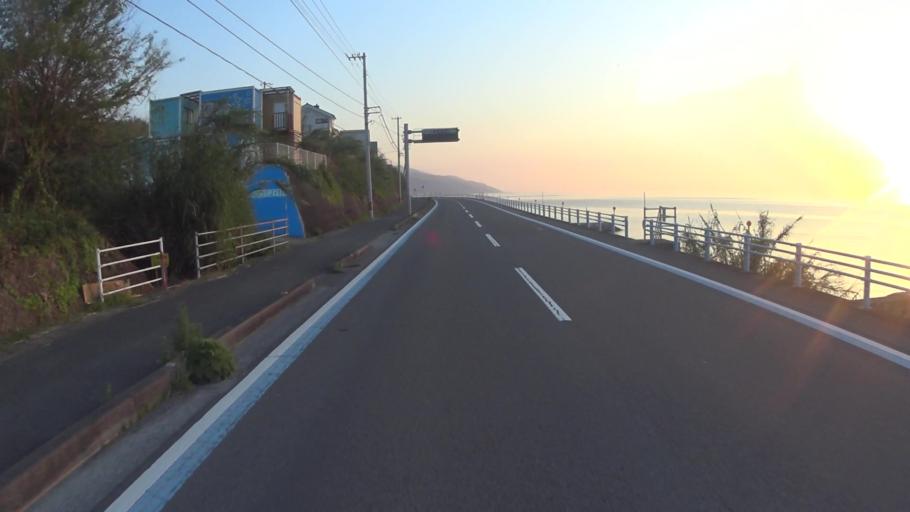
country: JP
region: Ehime
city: Iyo
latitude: 33.6742
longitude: 132.6148
